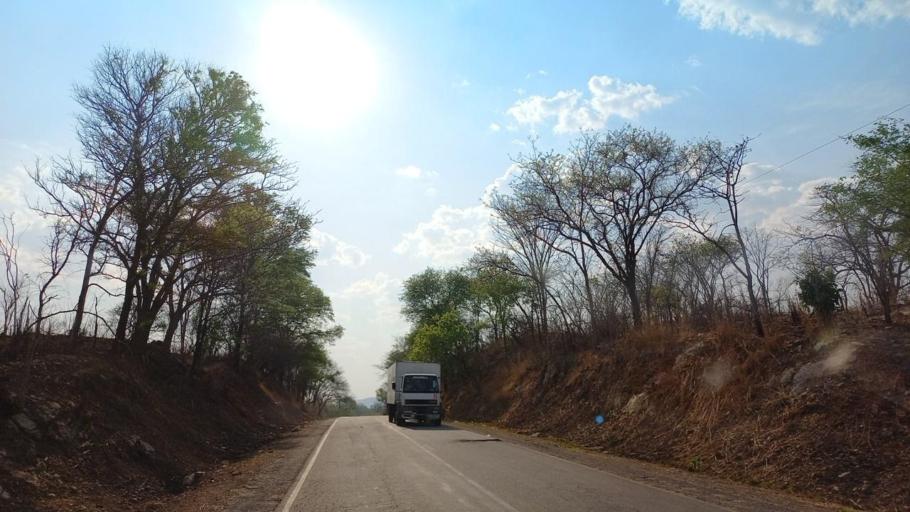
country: ZM
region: Lusaka
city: Luangwa
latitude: -14.9818
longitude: 30.1413
